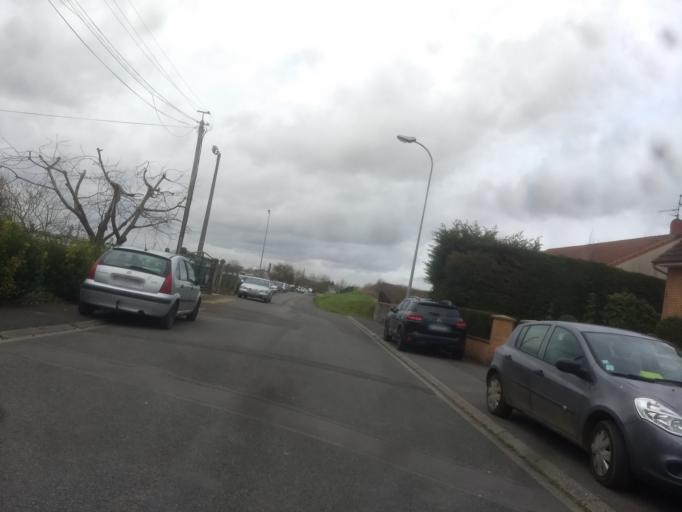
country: FR
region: Nord-Pas-de-Calais
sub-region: Departement du Pas-de-Calais
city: Sainte-Catherine
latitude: 50.3101
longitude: 2.7598
